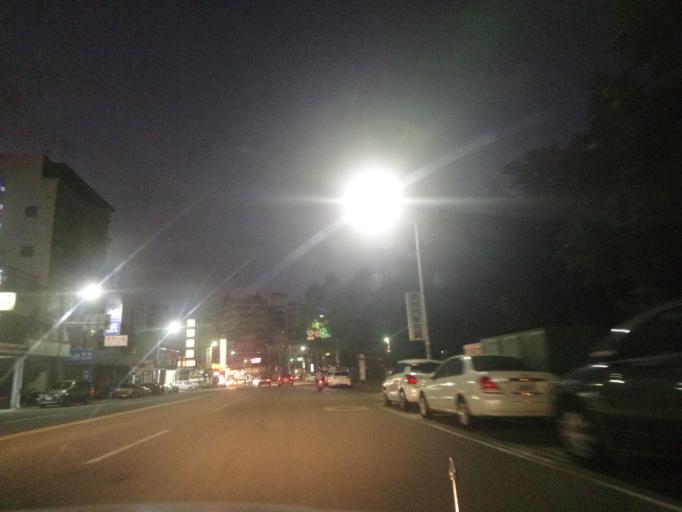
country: TW
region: Taiwan
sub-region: Hsinchu
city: Hsinchu
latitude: 24.8042
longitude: 120.9869
